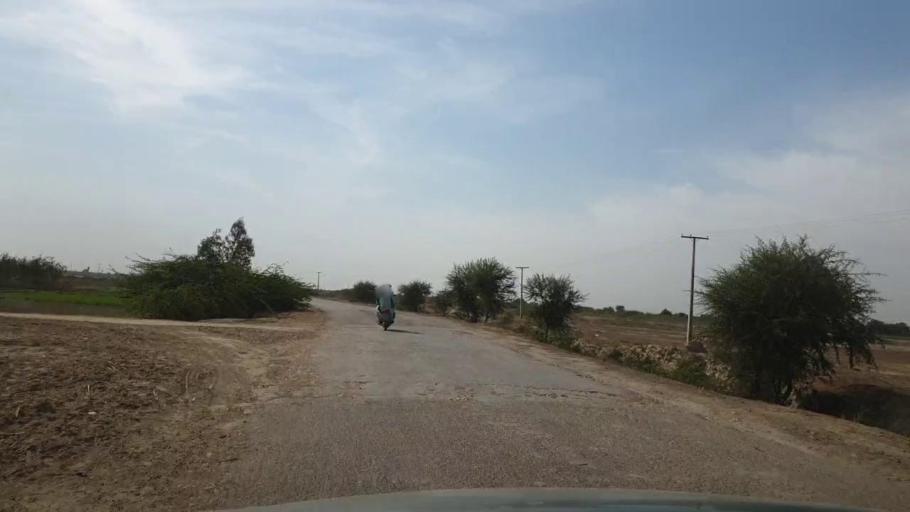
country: PK
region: Sindh
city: Kunri
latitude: 25.1689
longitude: 69.5214
